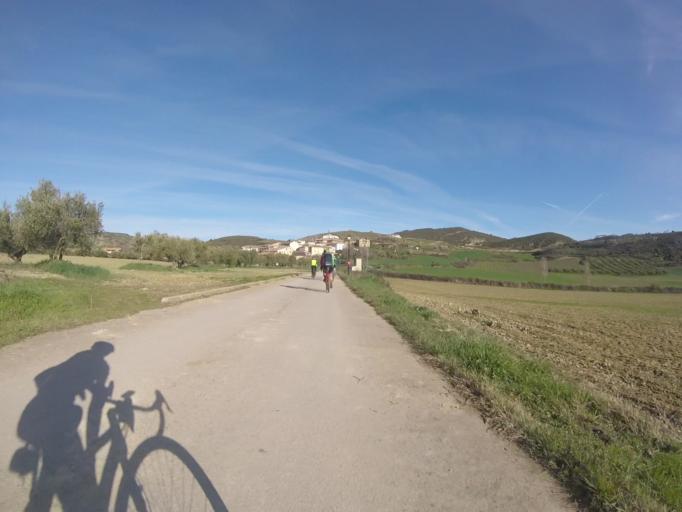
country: ES
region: Navarre
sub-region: Provincia de Navarra
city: Yerri
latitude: 42.6917
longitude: -1.9579
